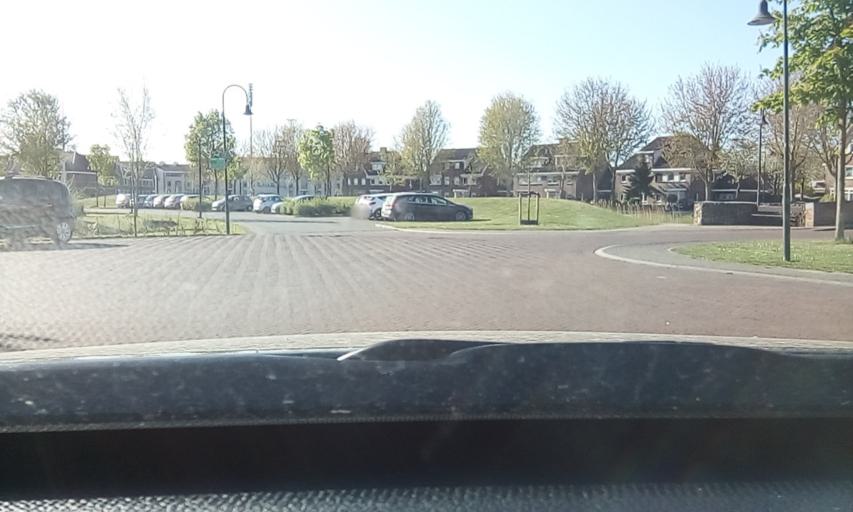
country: NL
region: Gelderland
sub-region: Gemeente Beuningen
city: Beuningen
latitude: 51.8510
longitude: 5.7683
